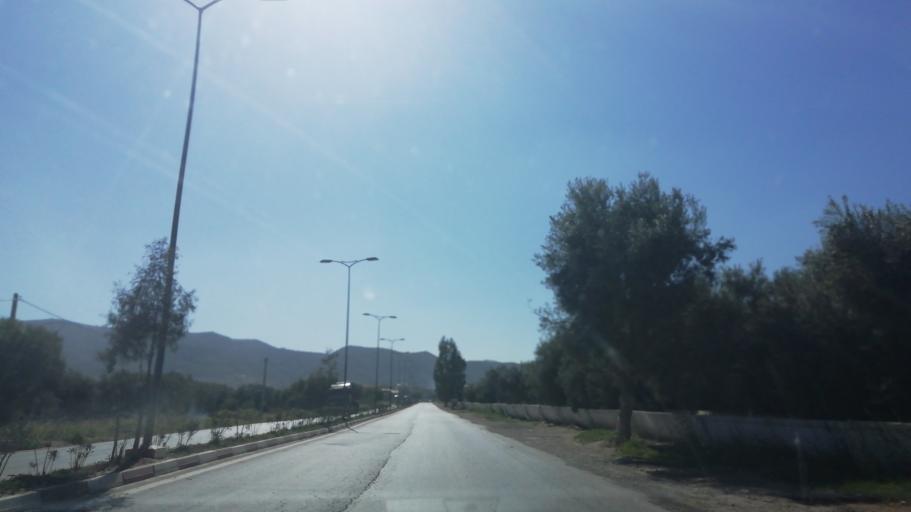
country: DZ
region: Mascara
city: Sig
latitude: 35.5342
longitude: -0.2033
